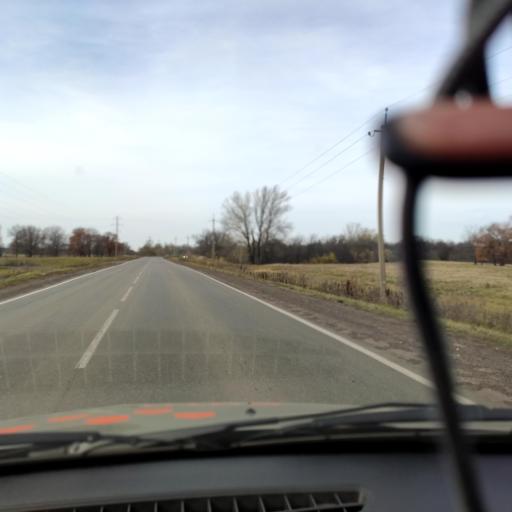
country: RU
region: Bashkortostan
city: Kabakovo
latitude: 54.5632
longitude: 55.9970
